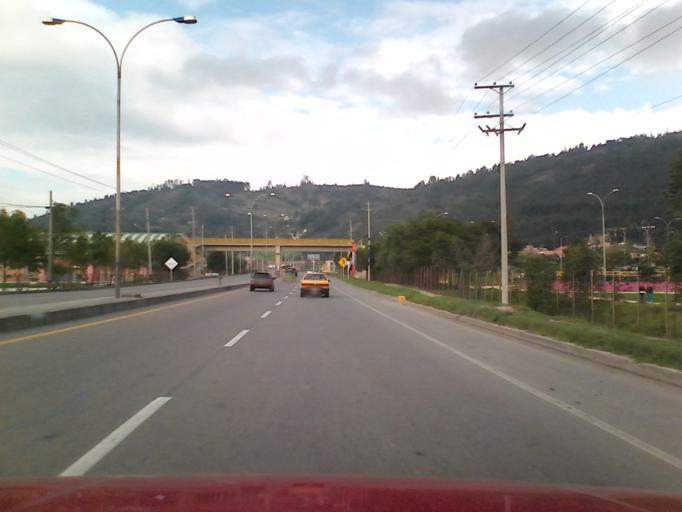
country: CO
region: Boyaca
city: Duitama
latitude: 5.8058
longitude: -73.0339
